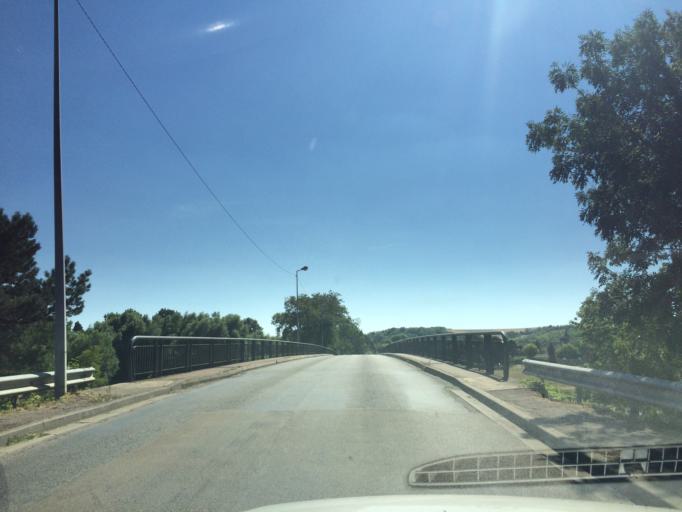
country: FR
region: Bourgogne
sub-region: Departement de l'Yonne
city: Cheny
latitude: 47.9273
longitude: 3.5196
